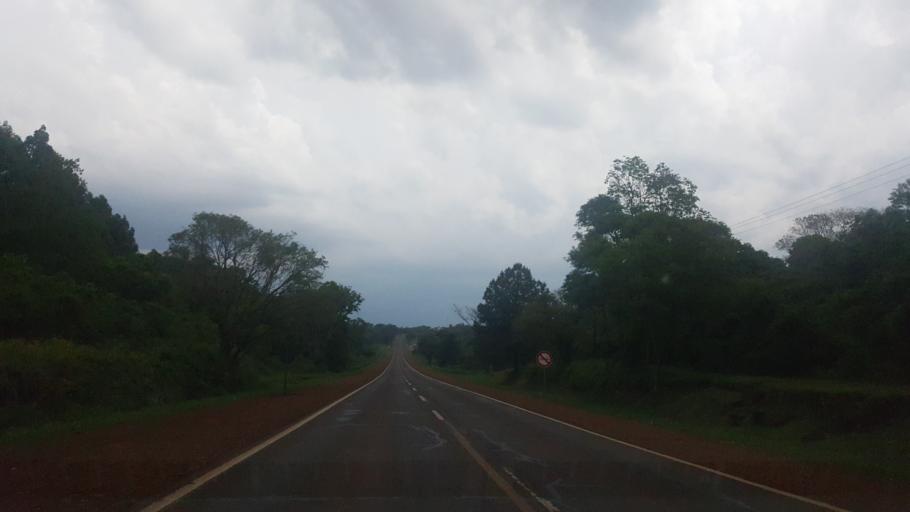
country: AR
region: Misiones
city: Santo Pipo
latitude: -27.1376
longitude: -55.3993
